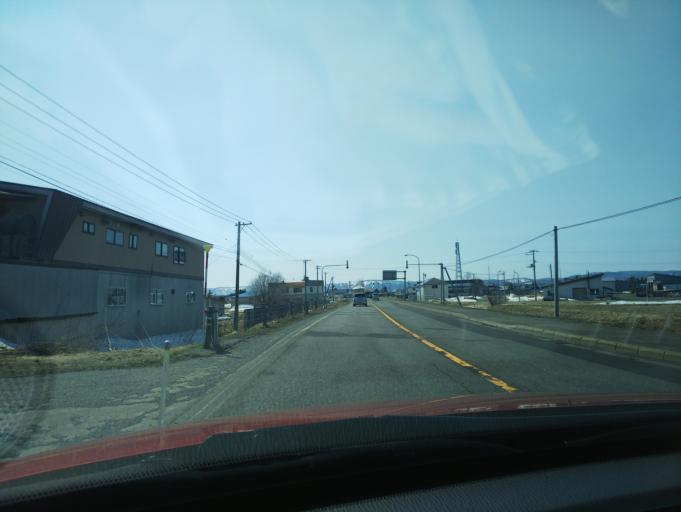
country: JP
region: Hokkaido
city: Nayoro
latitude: 44.2983
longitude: 142.4279
